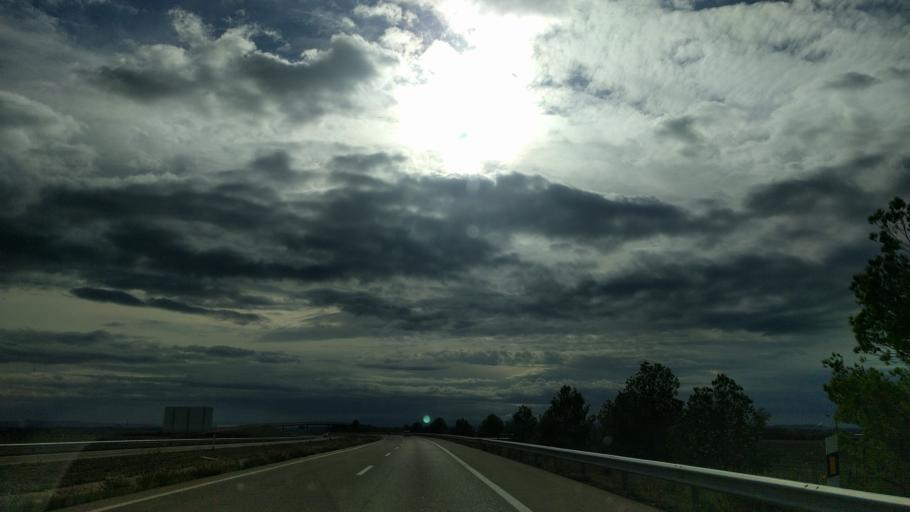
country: ES
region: Aragon
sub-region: Provincia de Huesca
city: Igries
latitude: 42.2247
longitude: -0.4432
